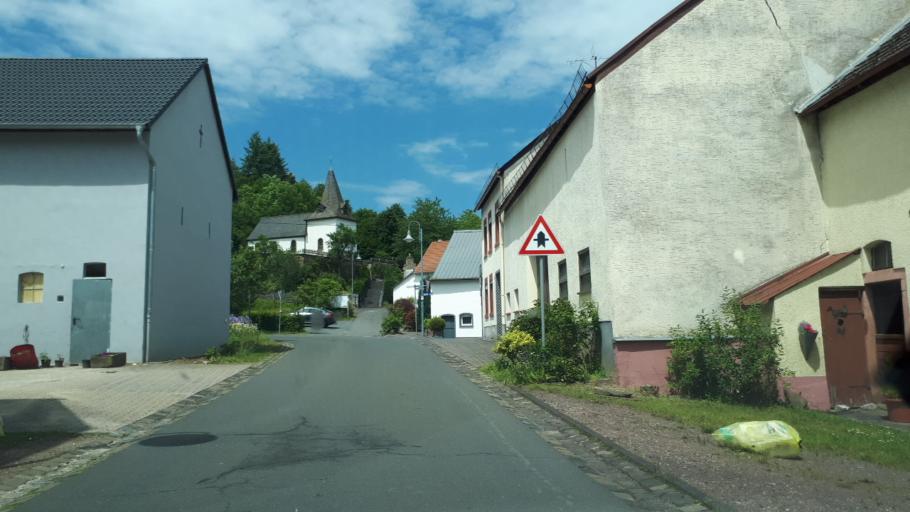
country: DE
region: Rheinland-Pfalz
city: Immerath
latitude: 50.1310
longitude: 6.9566
